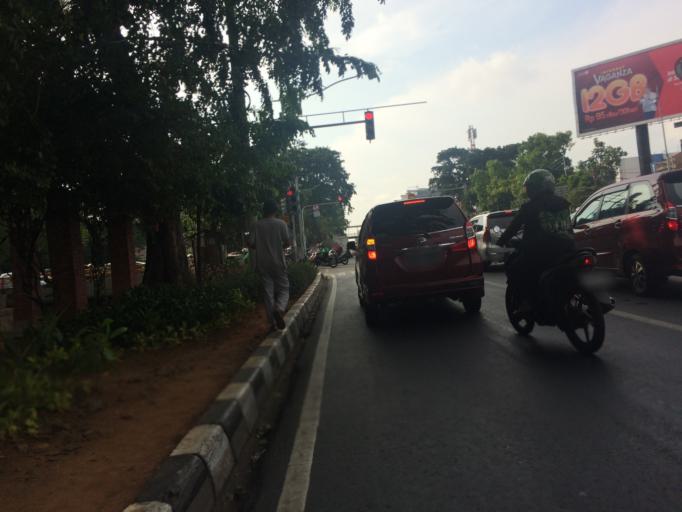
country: ID
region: Jakarta Raya
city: Jakarta
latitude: -6.1643
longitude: 106.8386
